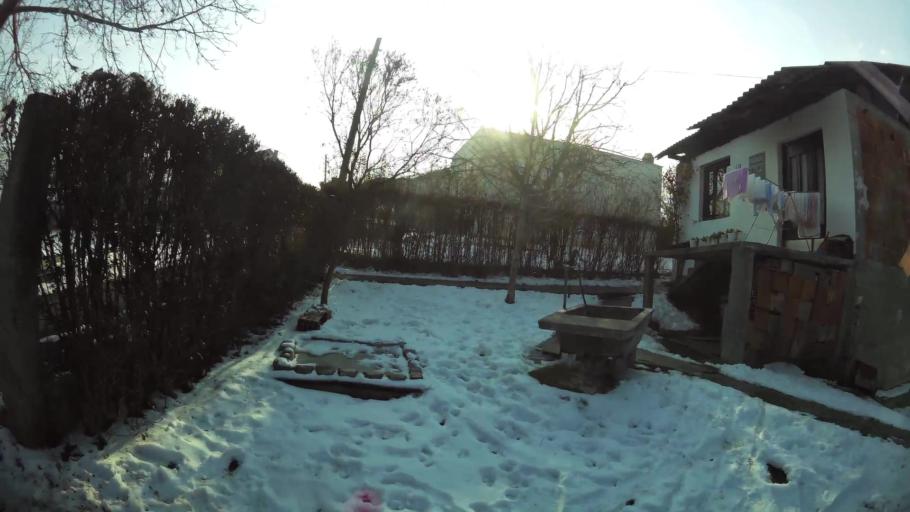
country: MK
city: Creshevo
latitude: 42.0167
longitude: 21.5046
